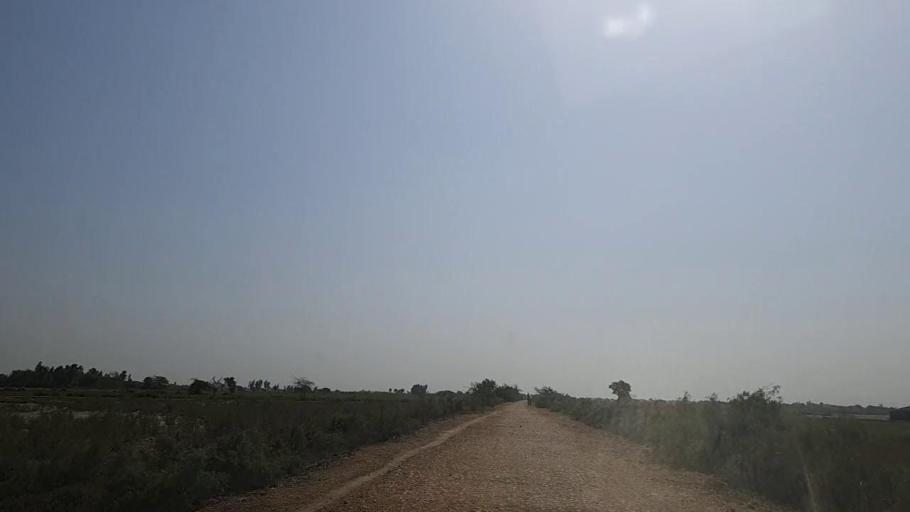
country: PK
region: Sindh
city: Daro Mehar
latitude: 24.7124
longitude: 68.1217
